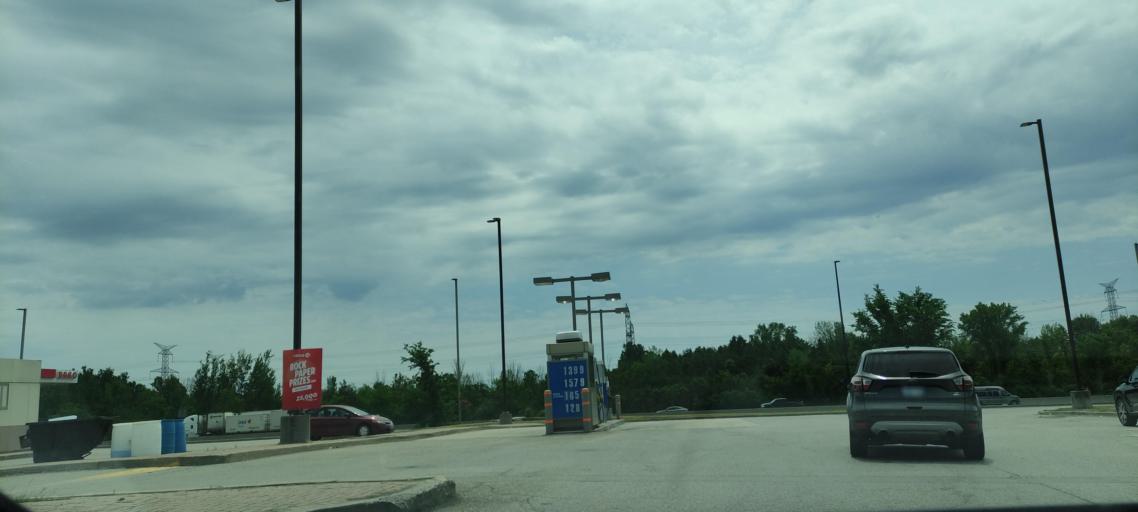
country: CA
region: Ontario
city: Oshawa
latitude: 43.9209
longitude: -78.5413
